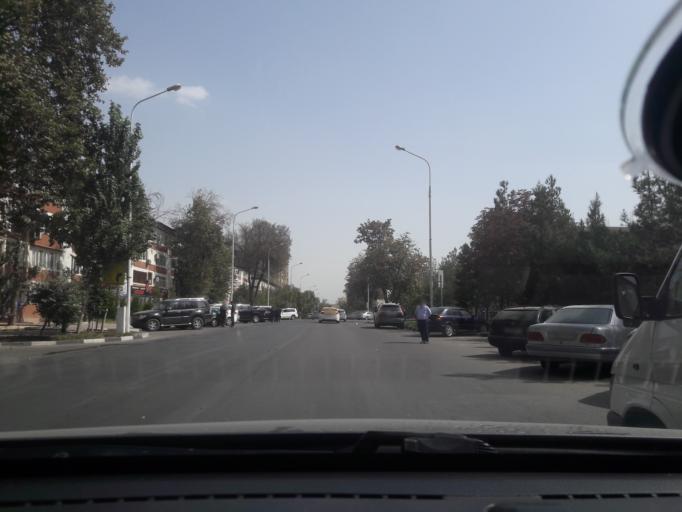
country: TJ
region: Dushanbe
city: Dushanbe
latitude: 38.5641
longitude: 68.7553
